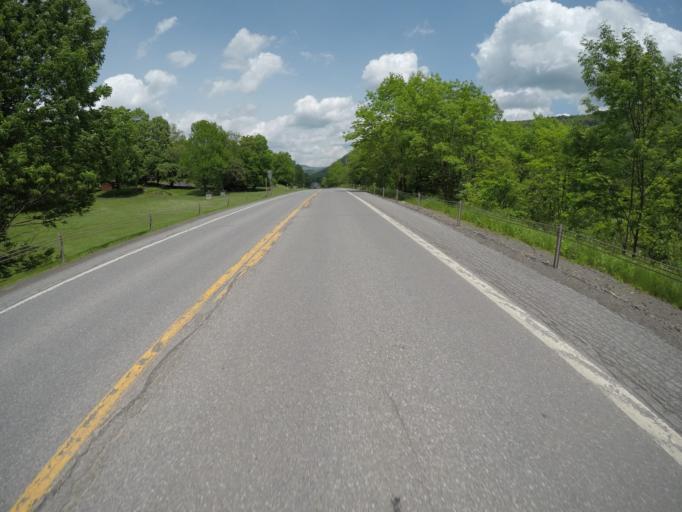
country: US
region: New York
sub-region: Delaware County
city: Stamford
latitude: 42.1638
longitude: -74.6198
